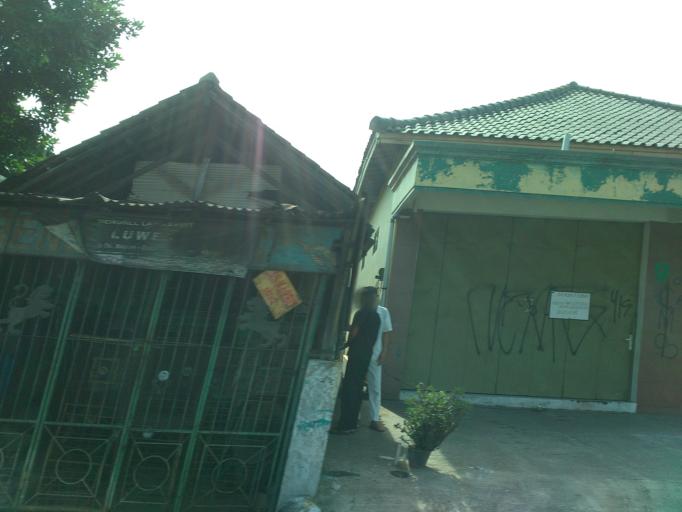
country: ID
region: Central Java
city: Ceper
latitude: -7.6488
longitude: 110.6853
